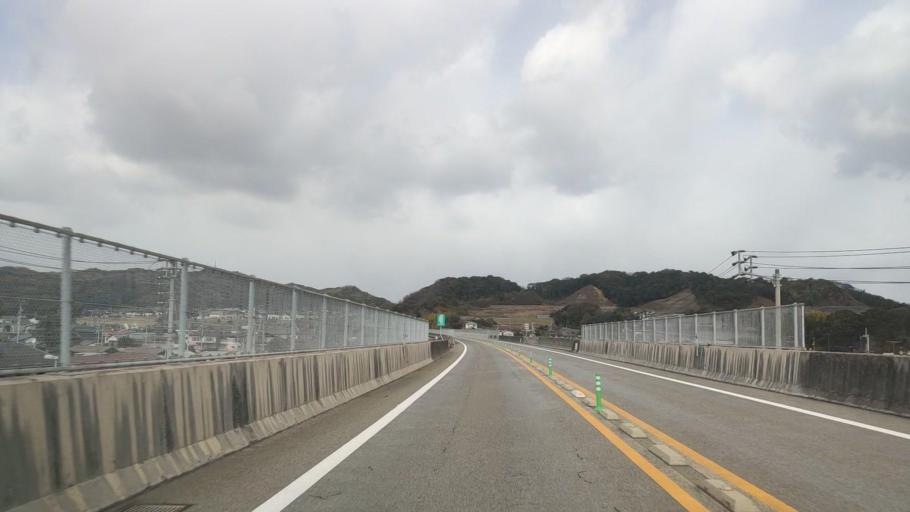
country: JP
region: Ehime
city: Hojo
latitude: 34.0605
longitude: 132.9722
